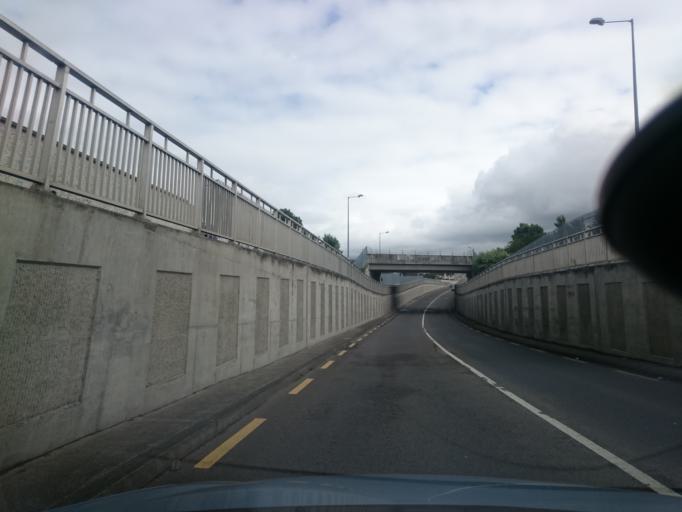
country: IE
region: Leinster
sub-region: County Carlow
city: Carlow
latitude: 52.8321
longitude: -6.9196
